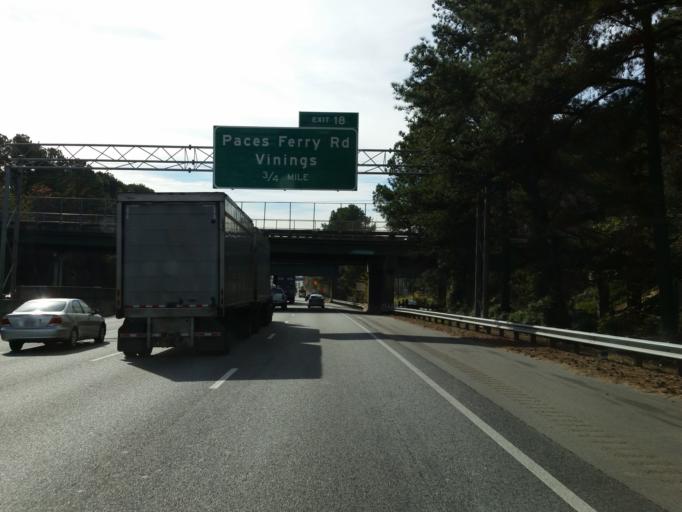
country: US
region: Georgia
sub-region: Cobb County
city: Vinings
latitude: 33.8807
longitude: -84.4730
